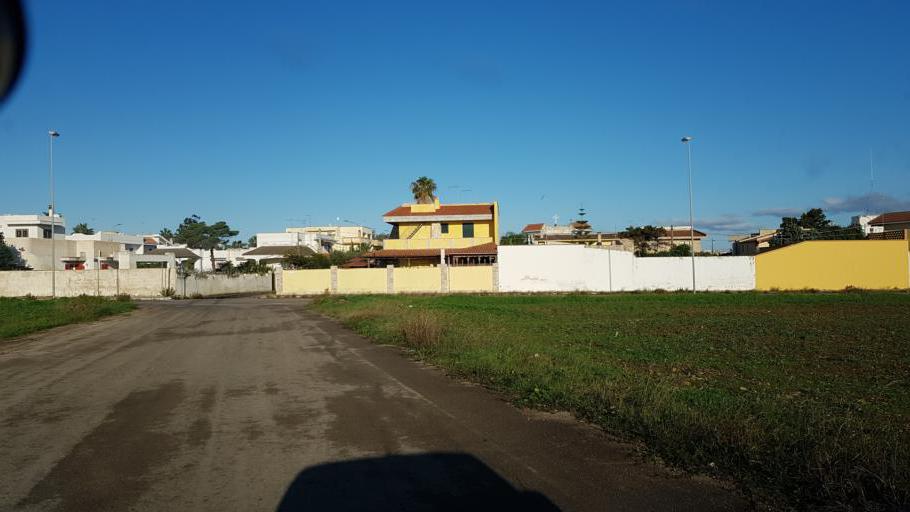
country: IT
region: Apulia
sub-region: Provincia di Brindisi
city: Torchiarolo
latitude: 40.5375
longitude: 18.0692
